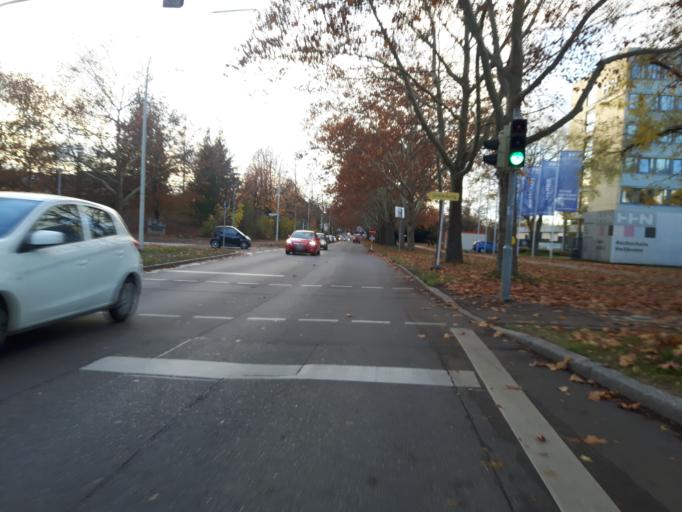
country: DE
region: Baden-Wuerttemberg
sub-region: Regierungsbezirk Stuttgart
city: Flein
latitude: 49.1215
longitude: 9.2120
